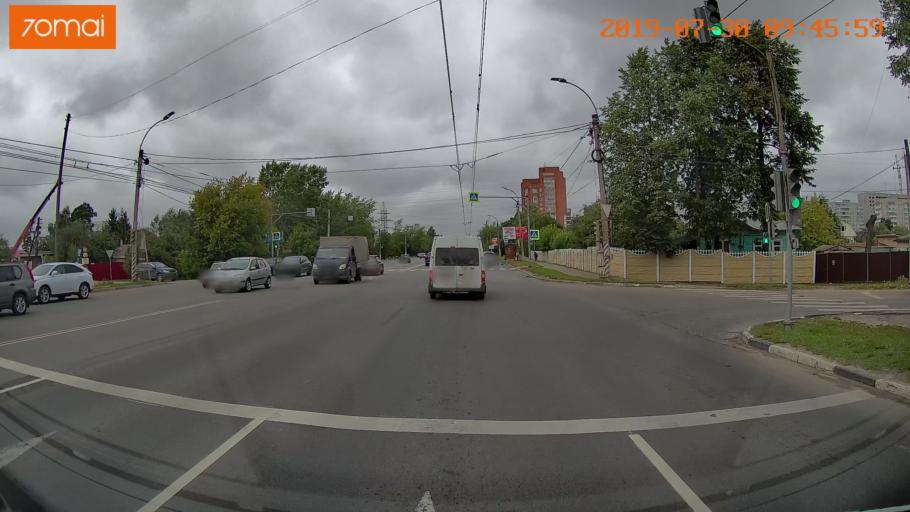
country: RU
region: Ivanovo
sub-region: Gorod Ivanovo
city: Ivanovo
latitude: 56.9522
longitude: 40.9751
